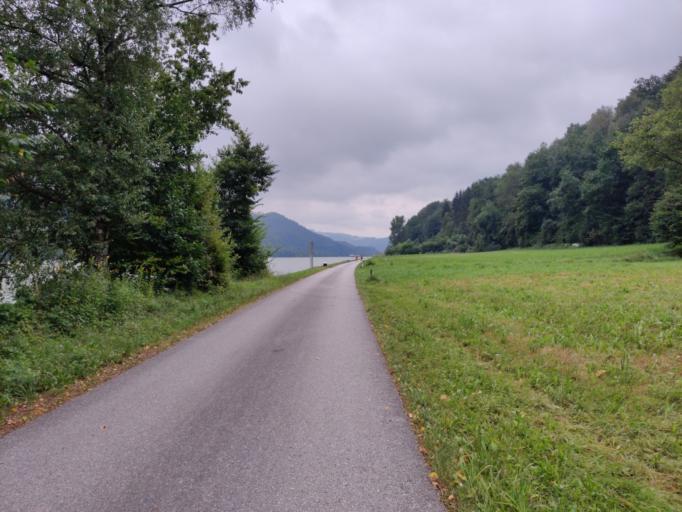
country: AT
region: Lower Austria
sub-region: Politischer Bezirk Melk
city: Nochling
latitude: 48.2270
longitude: 14.9416
